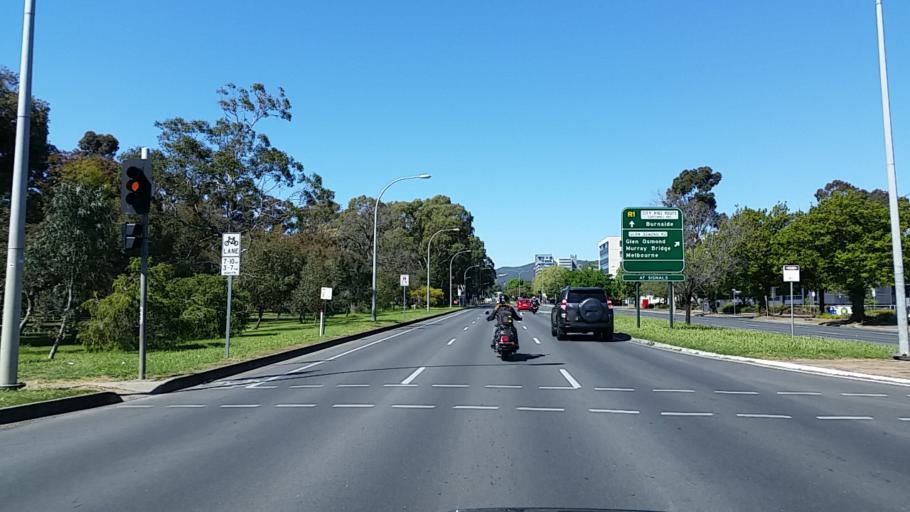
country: AU
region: South Australia
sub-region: Unley
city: Unley
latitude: -34.9405
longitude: 138.6128
